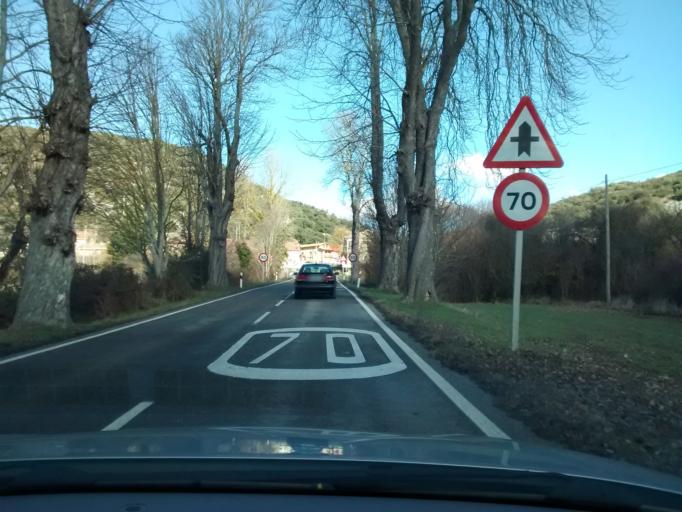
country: ES
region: Castille and Leon
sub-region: Provincia de Burgos
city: Medina de Pomar
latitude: 42.8910
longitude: -3.5943
